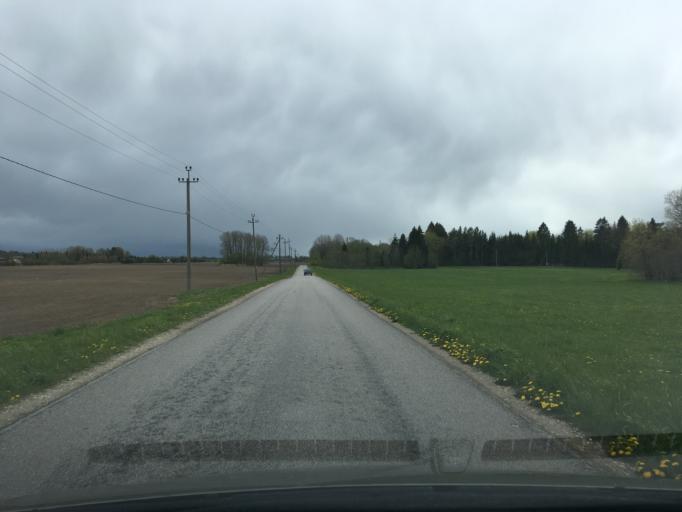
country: EE
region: Harju
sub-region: Joelaehtme vald
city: Loo
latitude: 59.3795
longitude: 24.9661
